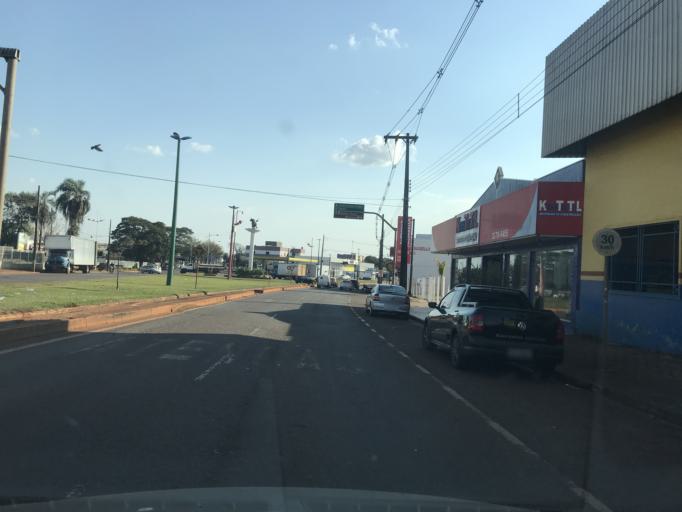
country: BR
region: Parana
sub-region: Toledo
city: Toledo
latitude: -24.7196
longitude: -53.7150
